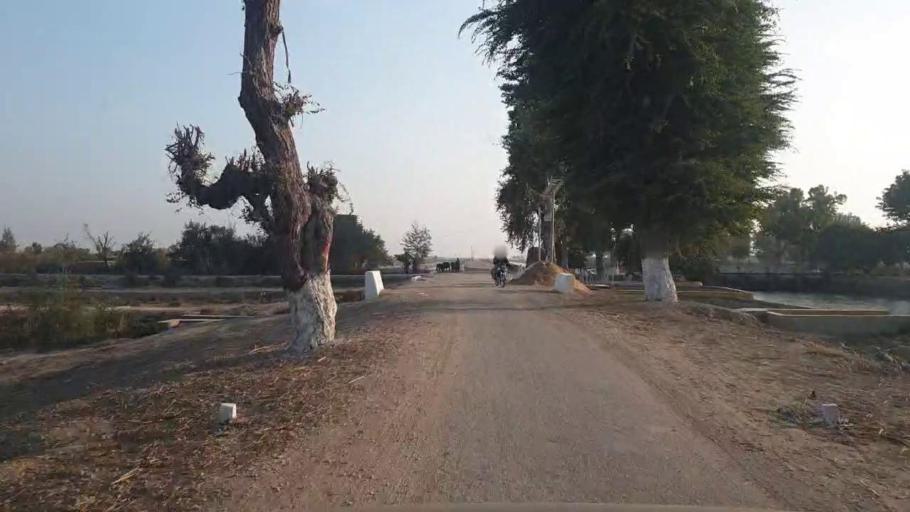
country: PK
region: Sindh
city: Shahdadpur
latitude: 25.8737
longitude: 68.5486
